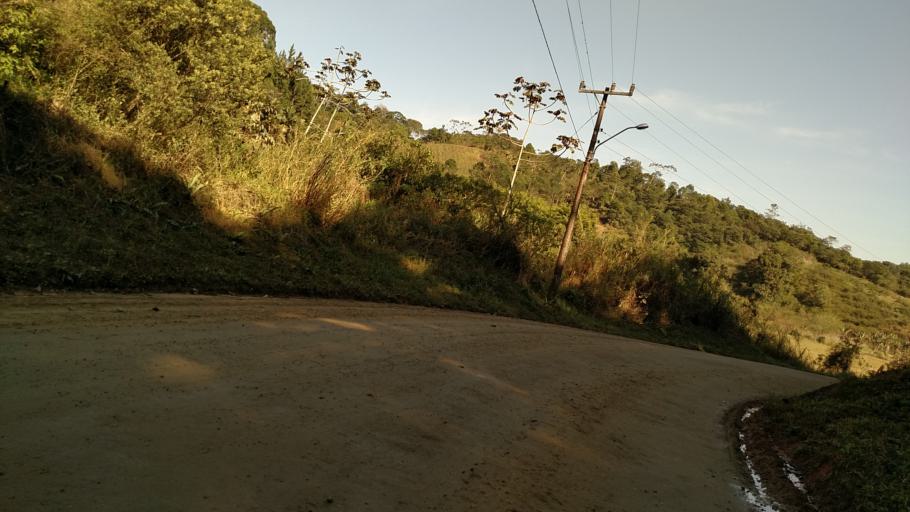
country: BR
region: Santa Catarina
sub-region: Pomerode
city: Pomerode
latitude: -26.7343
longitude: -49.0772
